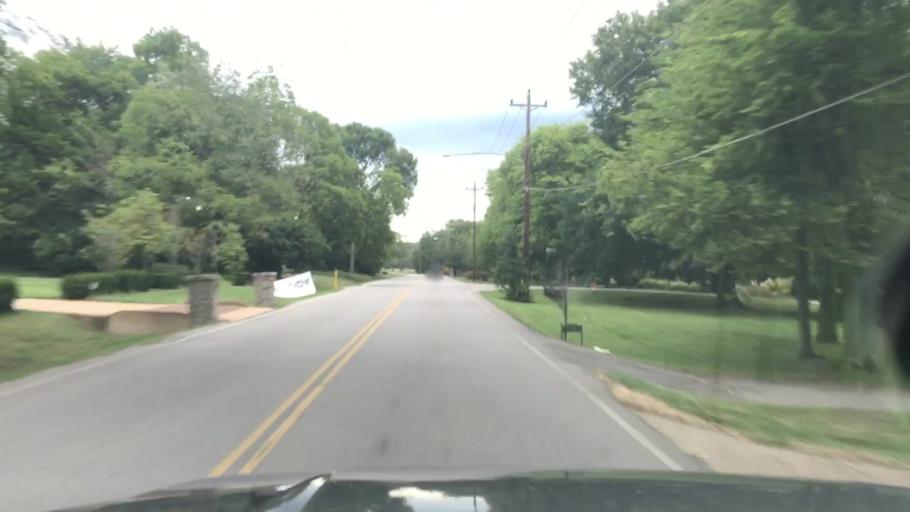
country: US
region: Tennessee
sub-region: Davidson County
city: Belle Meade
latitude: 36.0834
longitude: -86.8485
